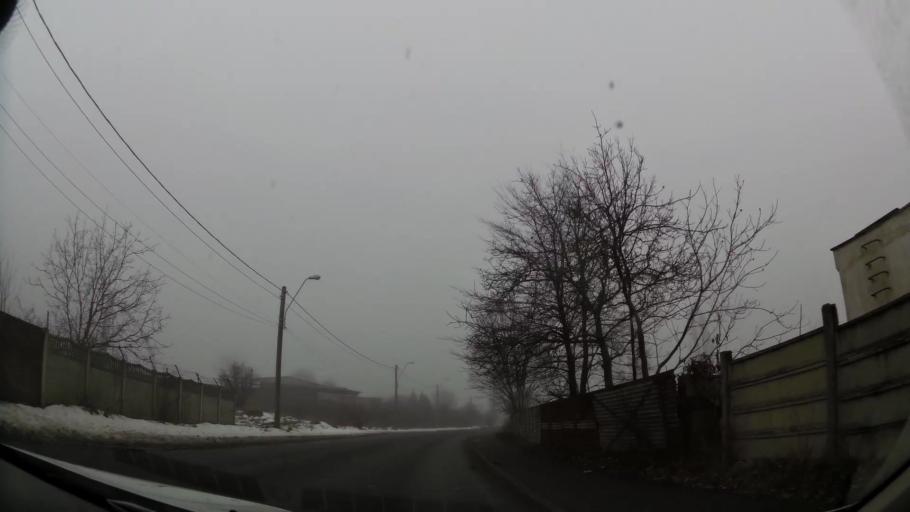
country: RO
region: Ilfov
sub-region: Comuna Chiajna
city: Rosu
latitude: 44.4763
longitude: 26.0075
